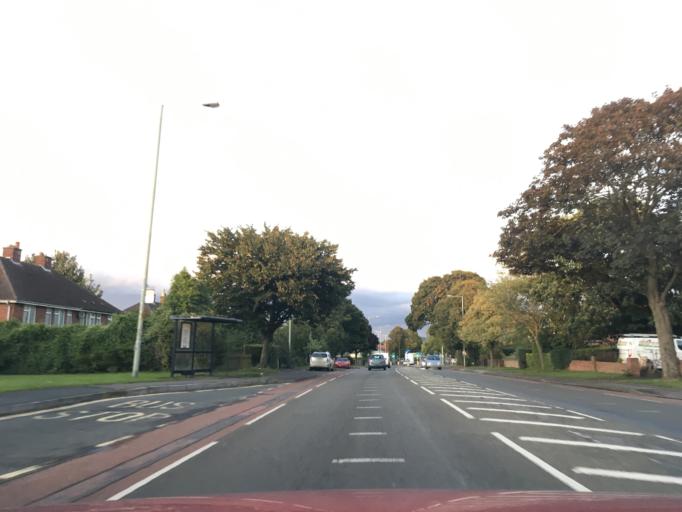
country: GB
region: England
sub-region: Gloucestershire
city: Gloucester
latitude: 51.8428
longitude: -2.2387
